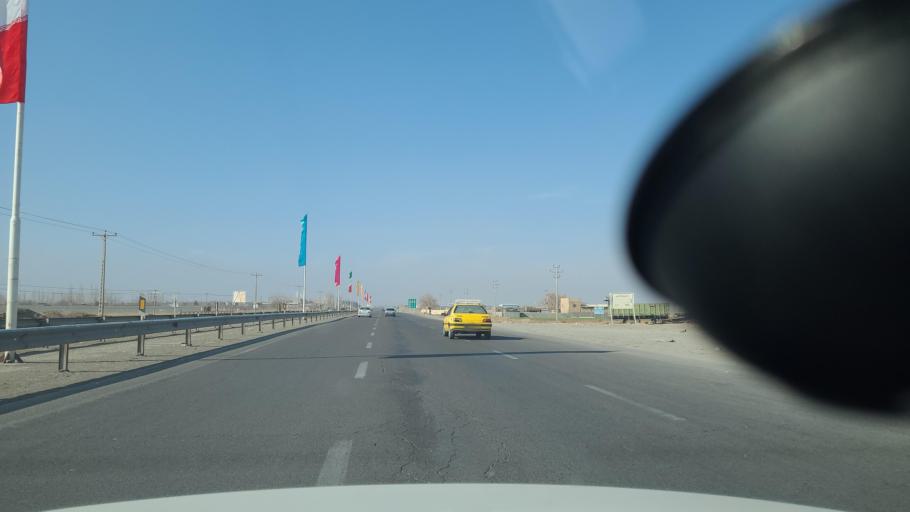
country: IR
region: Razavi Khorasan
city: Fariman
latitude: 35.7077
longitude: 59.8342
